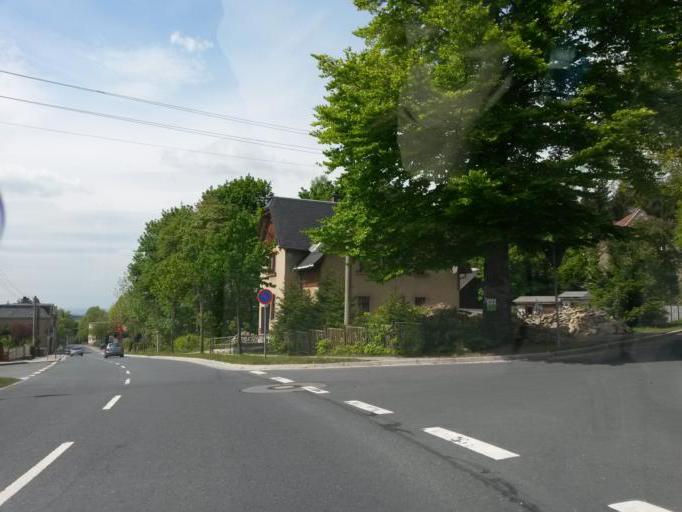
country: DE
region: Saxony
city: Pohl
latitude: 50.3941
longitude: 12.3420
